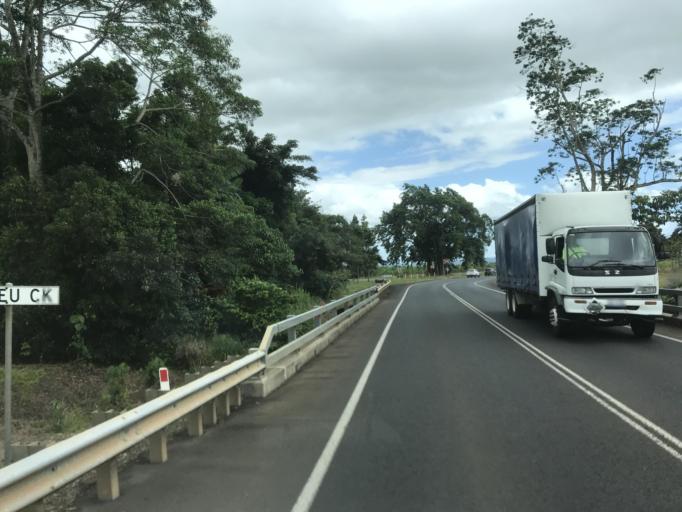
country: AU
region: Queensland
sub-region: Cassowary Coast
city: Innisfail
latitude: -17.5814
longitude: 146.0035
